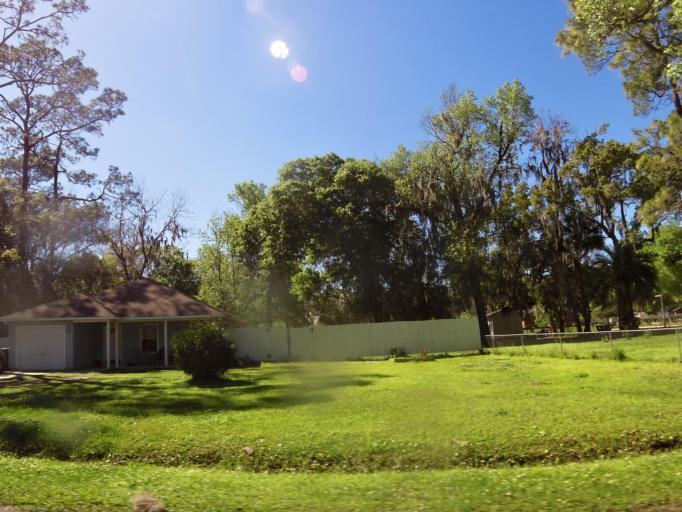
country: US
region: Florida
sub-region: Bradford County
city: Starke
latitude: 29.9455
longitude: -82.1055
